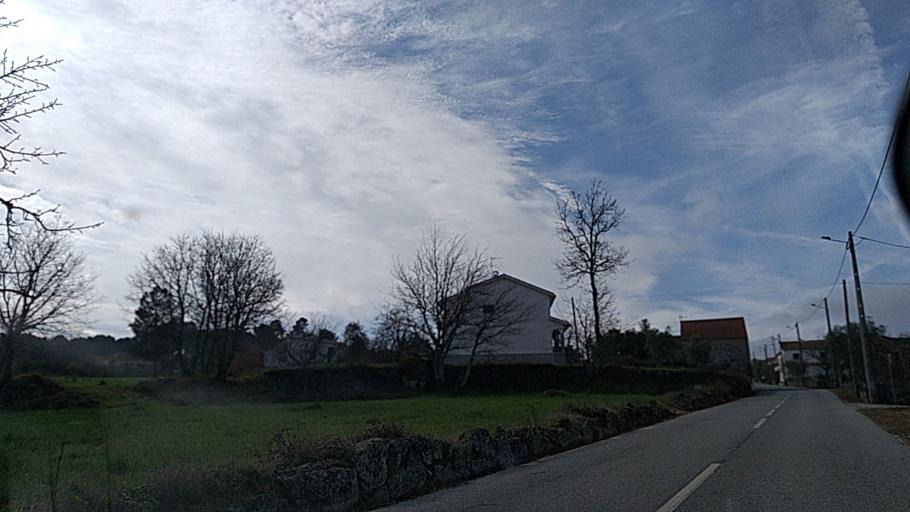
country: PT
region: Guarda
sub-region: Fornos de Algodres
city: Fornos de Algodres
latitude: 40.6586
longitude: -7.5333
